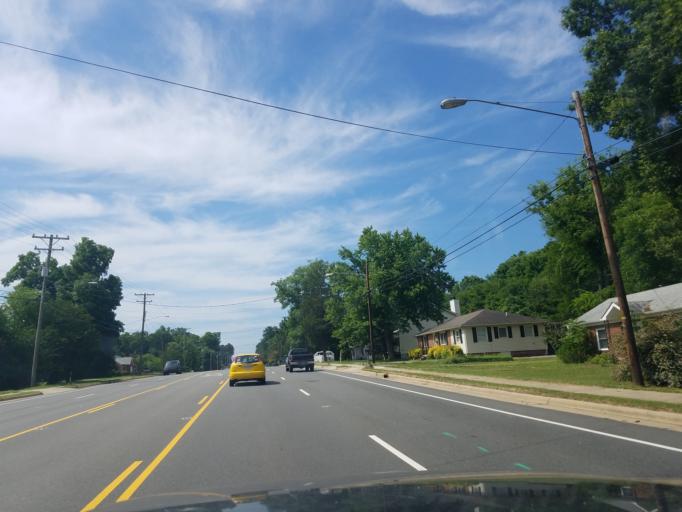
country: US
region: North Carolina
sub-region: Durham County
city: Durham
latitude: 36.0495
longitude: -78.9294
